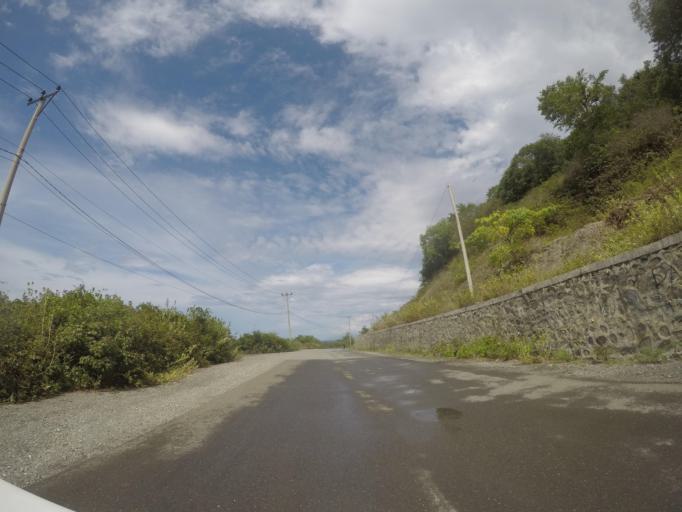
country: TL
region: Liquica
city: Maubara
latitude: -8.6327
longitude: 125.1480
